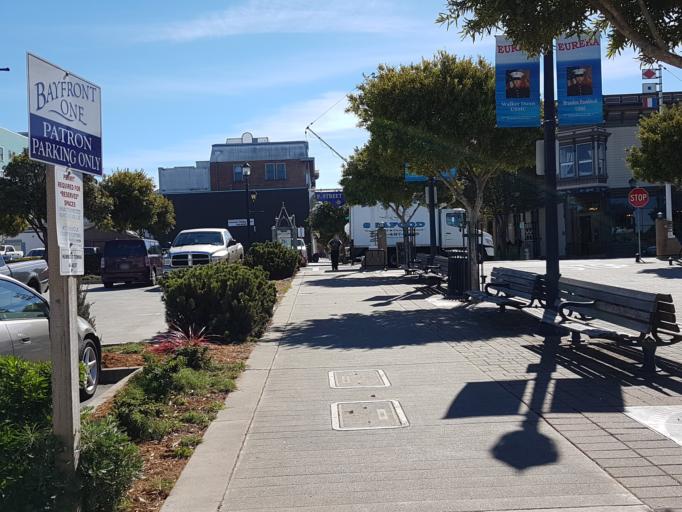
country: US
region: California
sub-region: Humboldt County
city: Eureka
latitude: 40.8056
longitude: -124.1668
